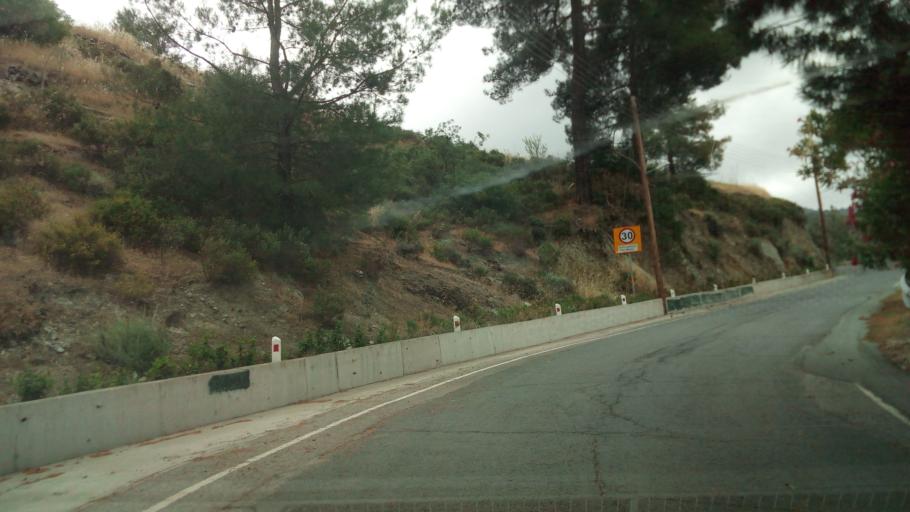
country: CY
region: Limassol
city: Pelendri
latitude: 34.8950
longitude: 33.0035
